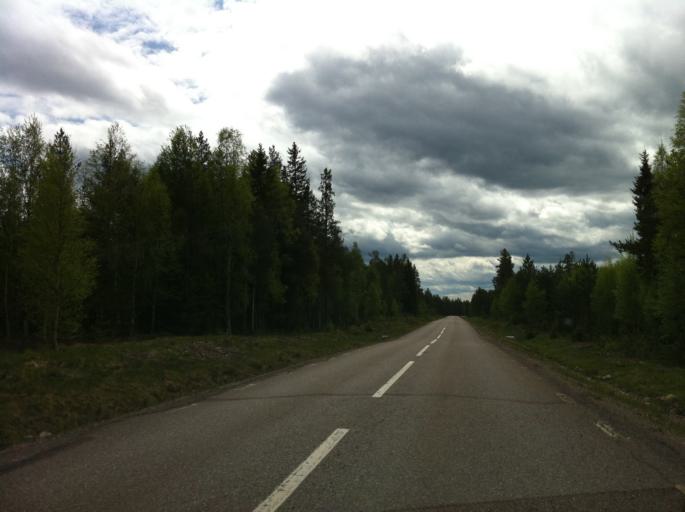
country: NO
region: Hedmark
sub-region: Trysil
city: Innbygda
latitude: 61.5361
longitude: 13.0819
